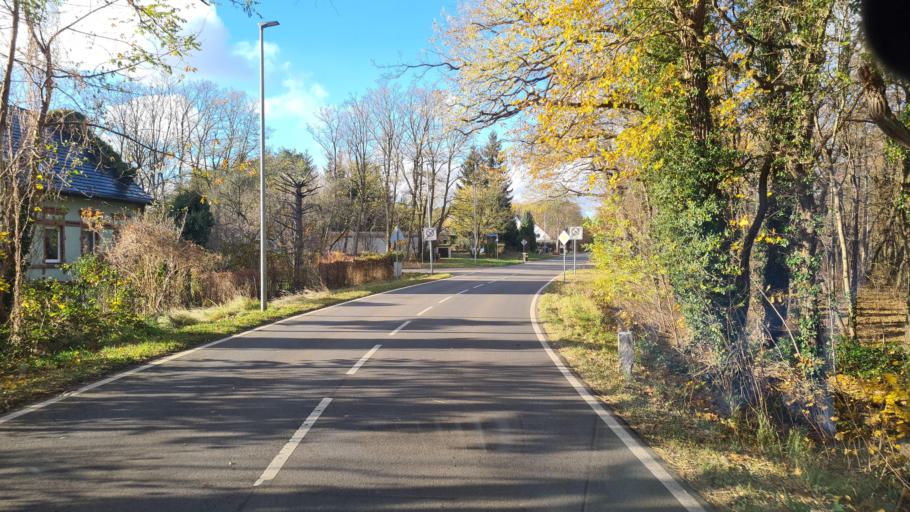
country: DE
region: Brandenburg
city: Spremberg
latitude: 51.5778
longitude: 14.3516
